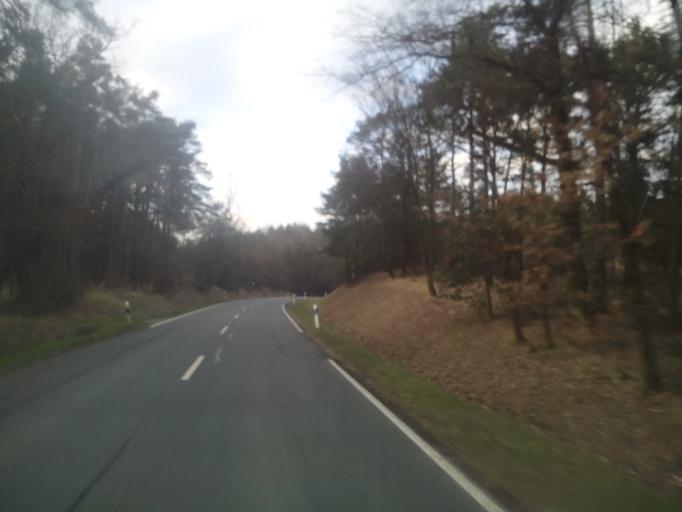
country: DE
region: Bavaria
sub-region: Upper Franconia
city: Pommersfelden
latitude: 49.7366
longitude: 10.8170
